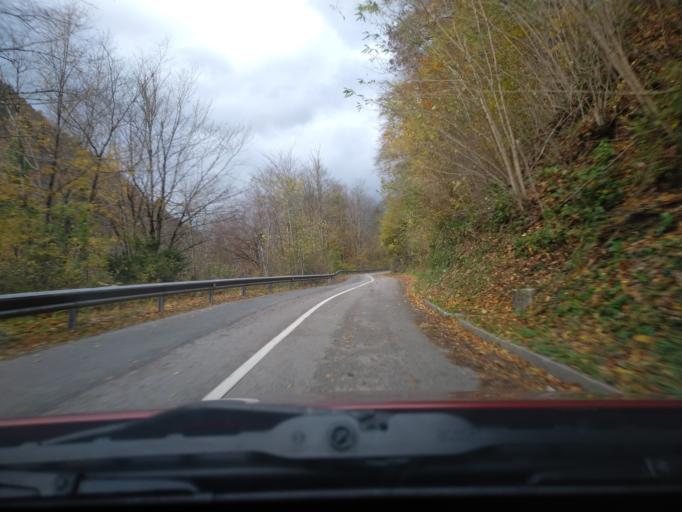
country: SI
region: Kamnik
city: Mekinje
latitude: 46.2923
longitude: 14.6152
